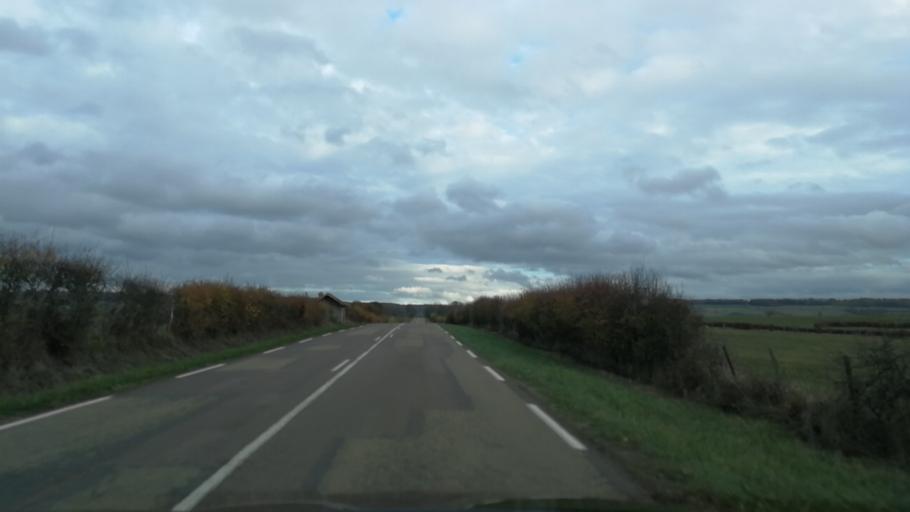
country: FR
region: Bourgogne
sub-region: Departement de la Cote-d'Or
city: Saulieu
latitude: 47.2693
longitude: 4.3744
